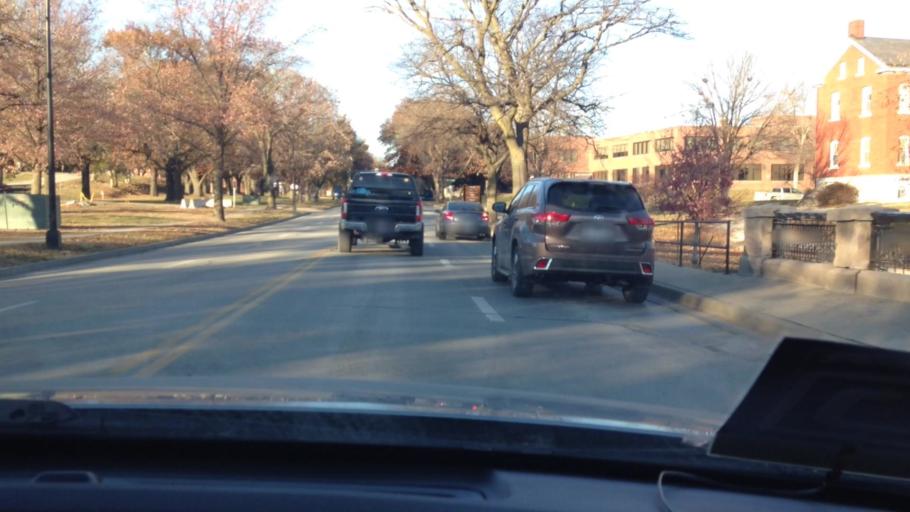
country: US
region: Kansas
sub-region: Leavenworth County
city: Leavenworth
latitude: 39.3470
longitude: -94.9196
